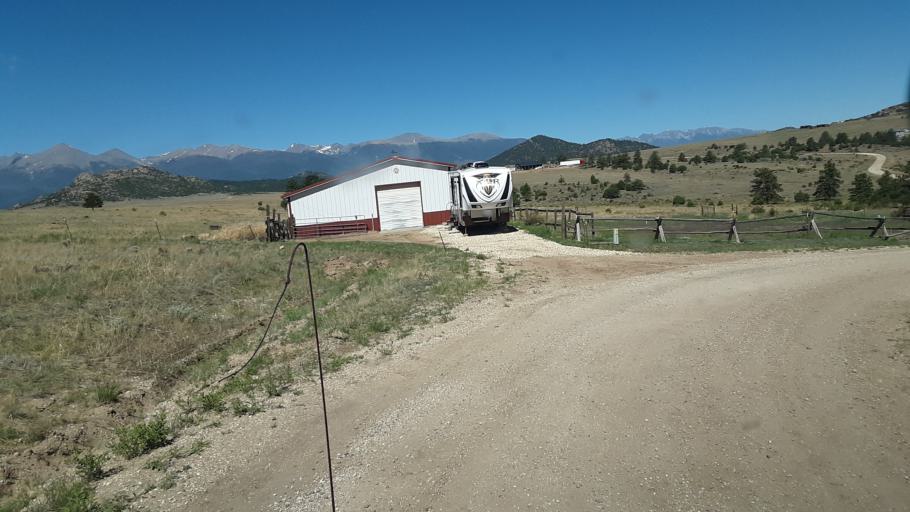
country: US
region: Colorado
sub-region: Custer County
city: Westcliffe
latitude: 38.2339
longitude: -105.4755
